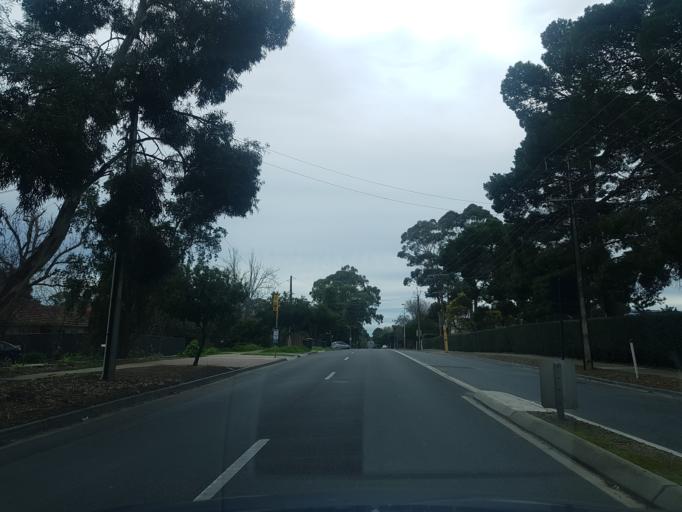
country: AU
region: South Australia
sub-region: Mitcham
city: Mitcham
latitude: -34.9762
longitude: 138.6273
